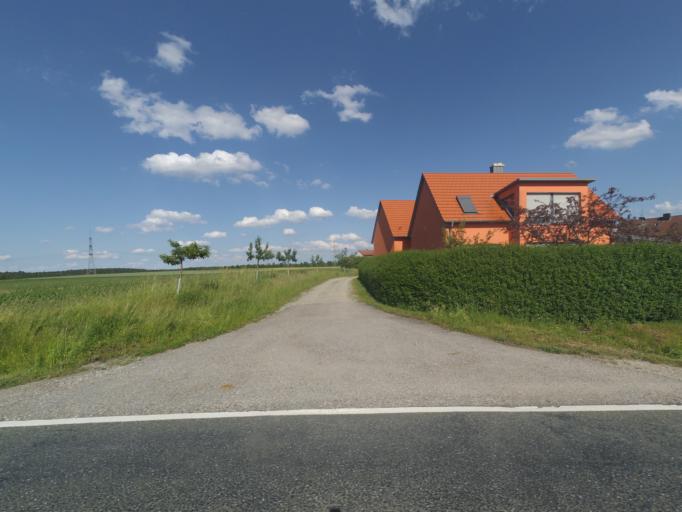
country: DE
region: Bavaria
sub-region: Regierungsbezirk Mittelfranken
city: Markt Erlbach
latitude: 49.4967
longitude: 10.6610
